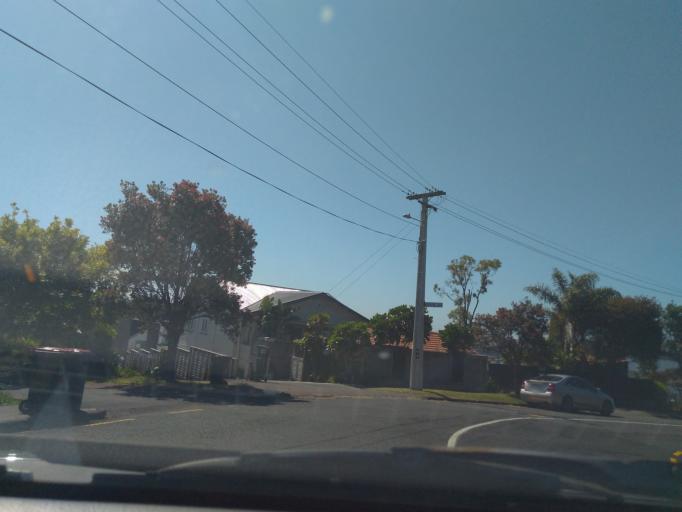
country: NZ
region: Auckland
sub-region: Auckland
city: Rosebank
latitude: -36.8831
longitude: 174.6964
